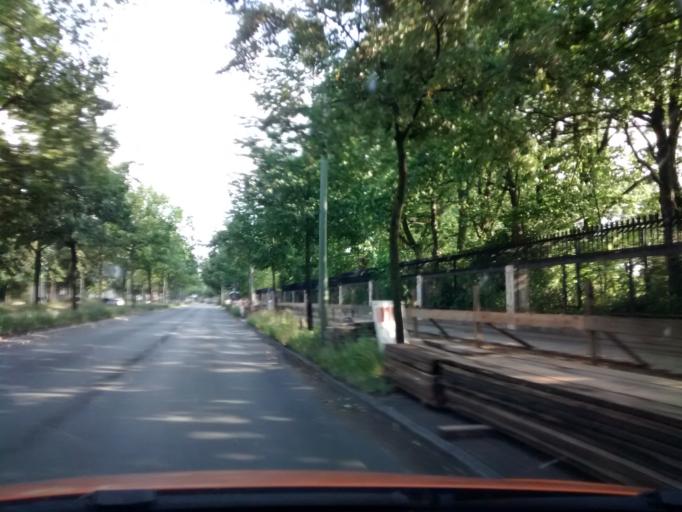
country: DE
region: Berlin
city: Lankwitz
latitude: 52.4268
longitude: 13.3556
